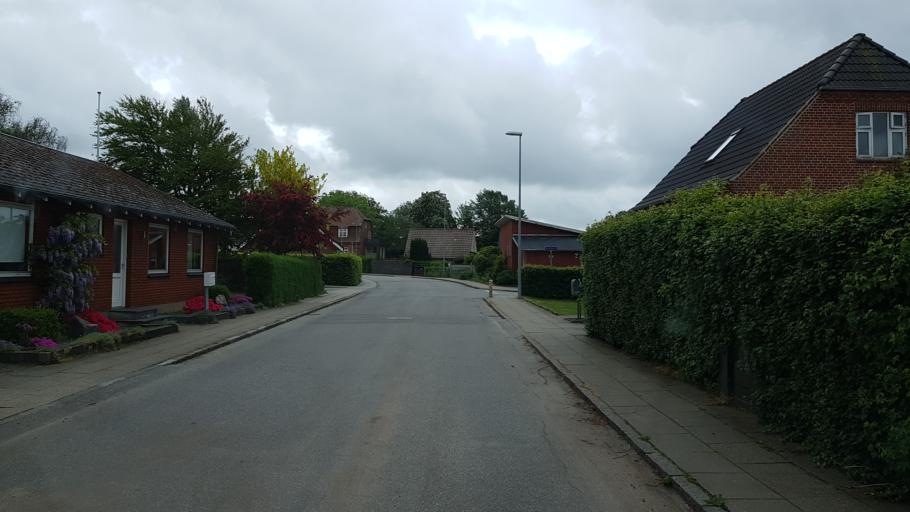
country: DK
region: Central Jutland
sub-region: Herning Kommune
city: Vildbjerg
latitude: 56.2002
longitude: 8.7643
